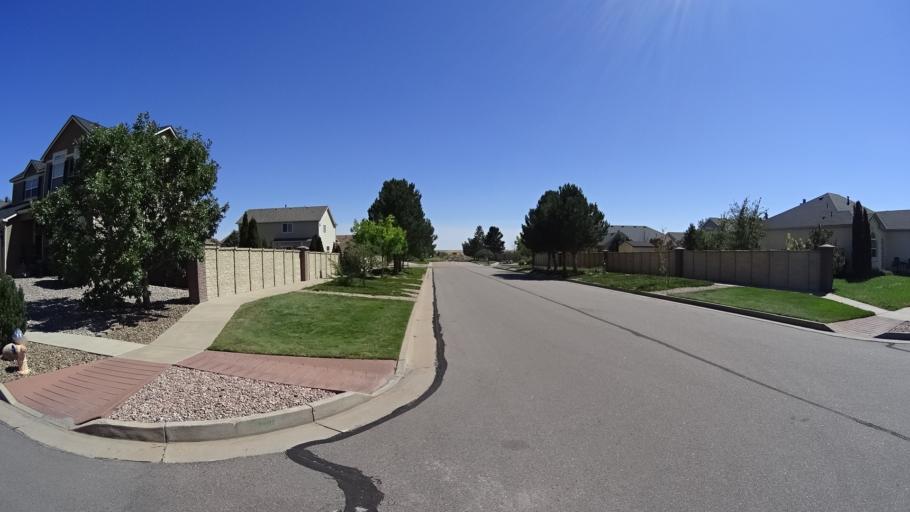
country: US
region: Colorado
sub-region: El Paso County
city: Security-Widefield
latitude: 38.7842
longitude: -104.7272
